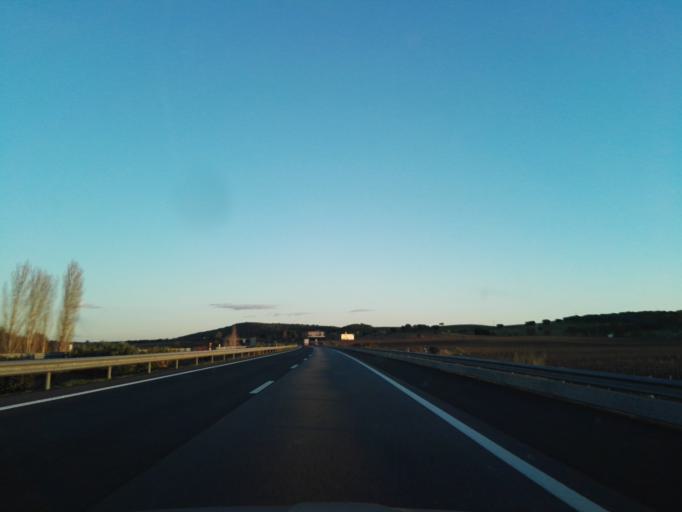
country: PT
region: Evora
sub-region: Montemor-O-Novo
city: Montemor-o-Novo
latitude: 38.6523
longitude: -8.1632
